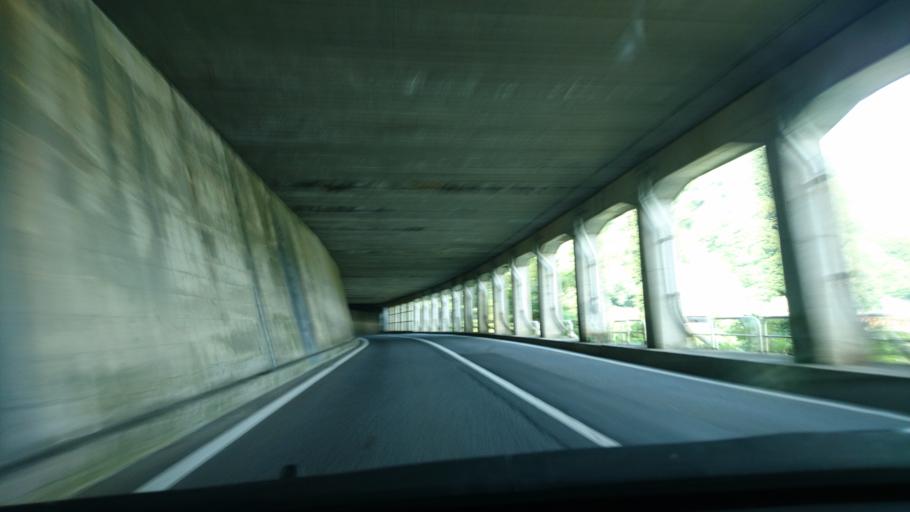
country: JP
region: Iwate
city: Kitakami
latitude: 39.3076
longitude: 140.8383
